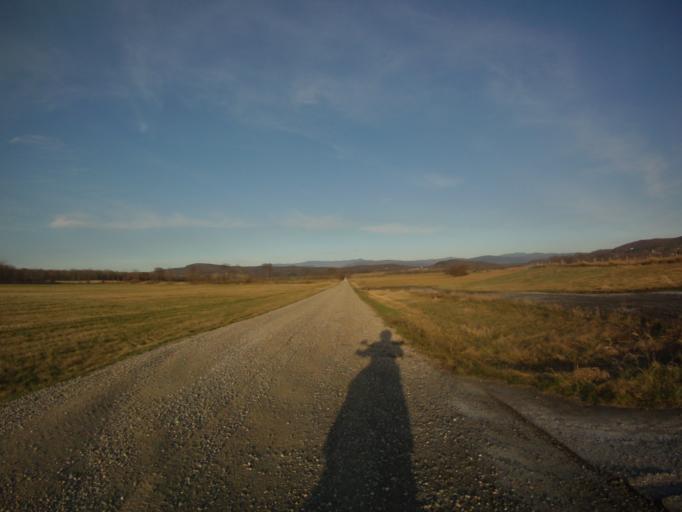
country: US
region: Vermont
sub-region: Addison County
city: Vergennes
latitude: 44.0992
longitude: -73.2944
